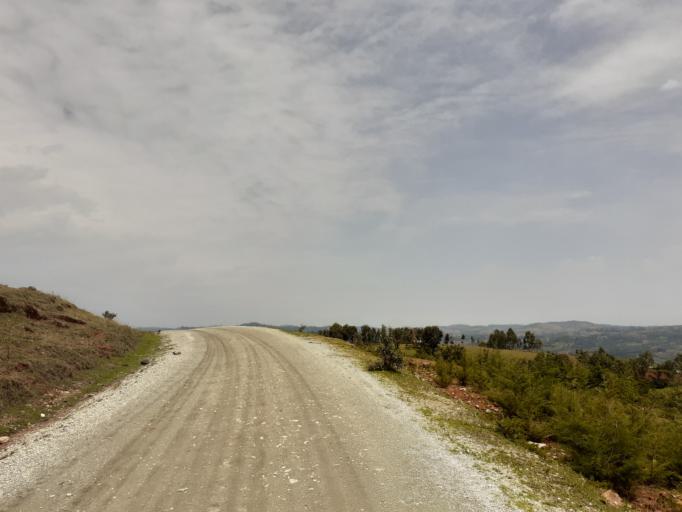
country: ET
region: Oromiya
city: Gimbi
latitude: 9.3531
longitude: 35.6903
